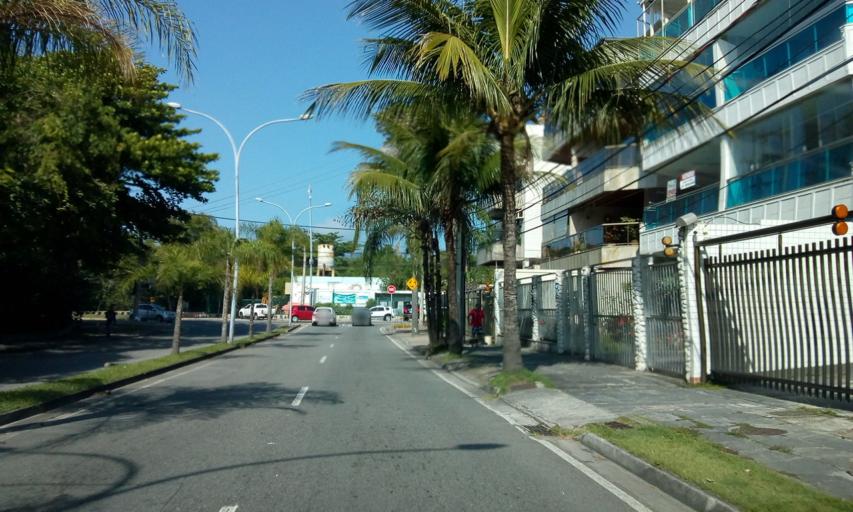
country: BR
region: Rio de Janeiro
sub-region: Nilopolis
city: Nilopolis
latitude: -23.0221
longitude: -43.4575
